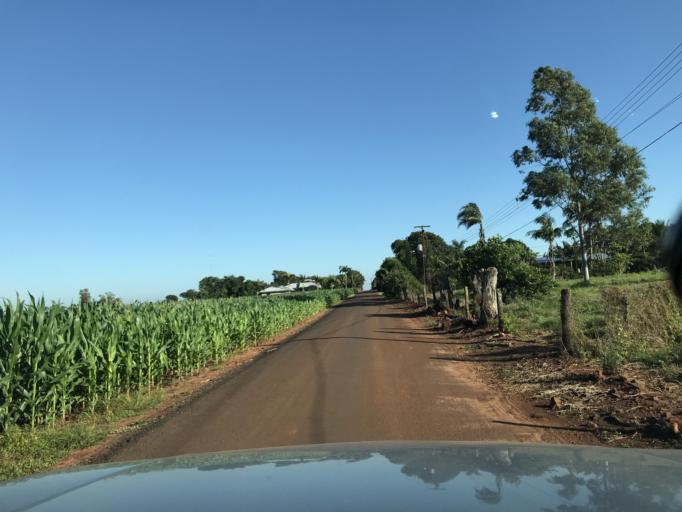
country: BR
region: Parana
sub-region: Palotina
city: Palotina
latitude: -24.2343
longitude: -53.7807
